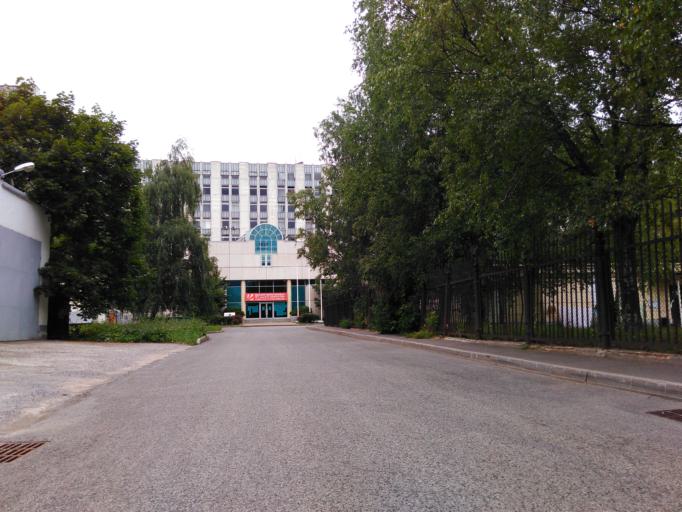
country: RU
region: Moscow
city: Vorob'yovo
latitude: 55.6977
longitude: 37.5326
